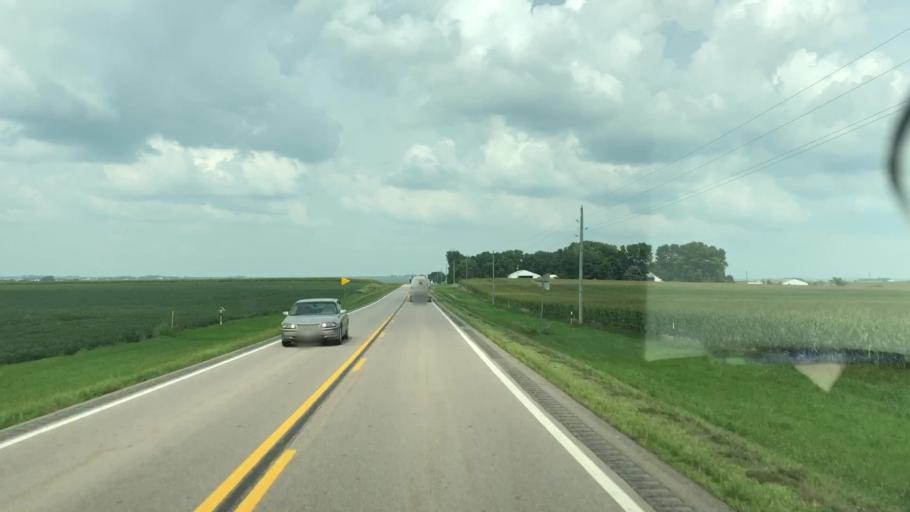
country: US
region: Iowa
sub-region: Plymouth County
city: Remsen
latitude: 42.7942
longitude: -95.9577
